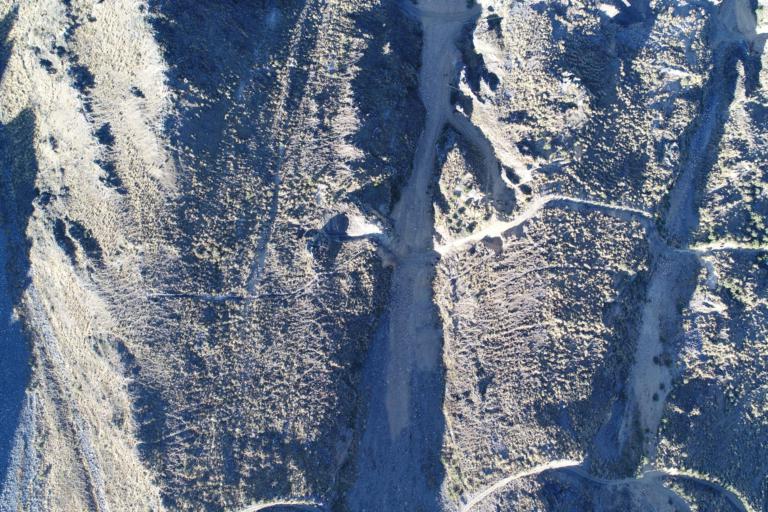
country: BO
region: La Paz
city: Viloco
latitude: -16.8188
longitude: -67.5484
